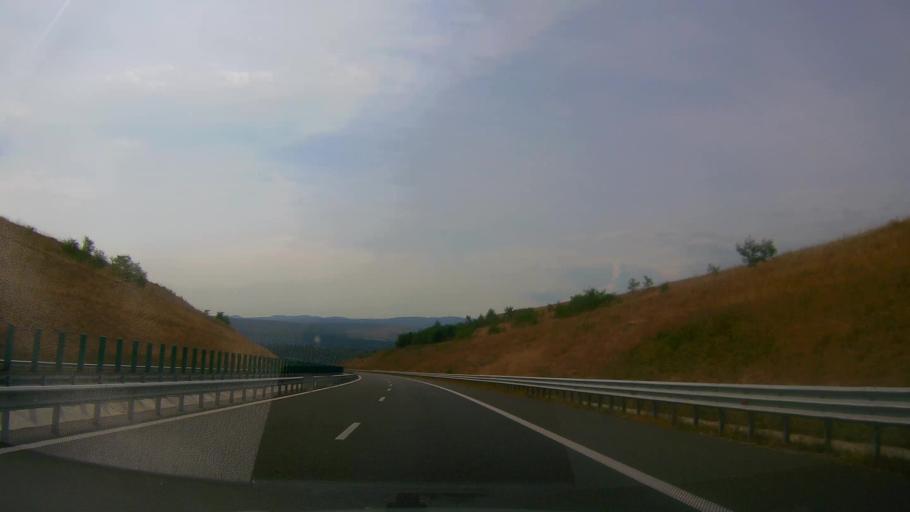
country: RO
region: Cluj
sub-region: Comuna Gilau
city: Gilau
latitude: 46.7722
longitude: 23.3843
